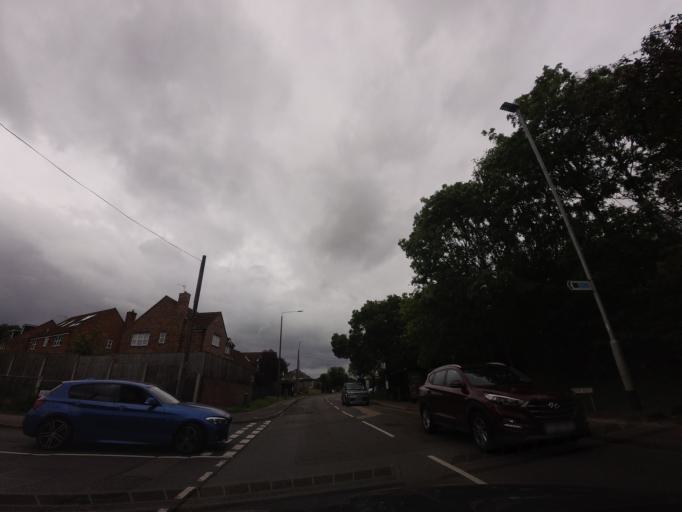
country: GB
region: England
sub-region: Nottinghamshire
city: Kimberley
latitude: 53.0030
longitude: -1.2492
